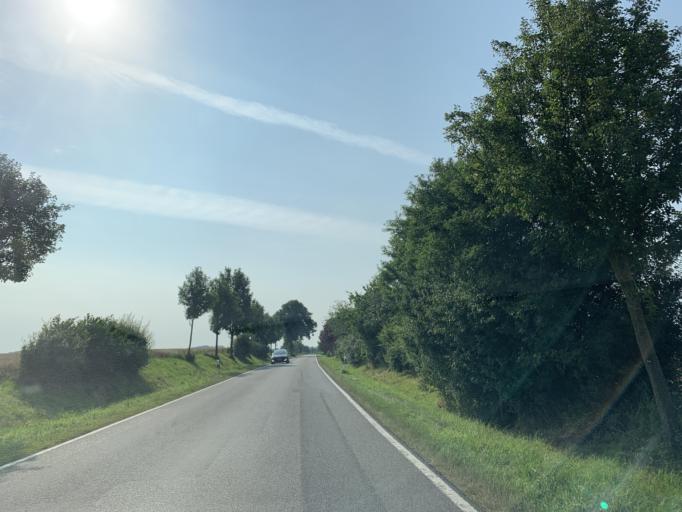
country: DE
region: Mecklenburg-Vorpommern
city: Blankensee
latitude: 53.4164
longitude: 13.2189
